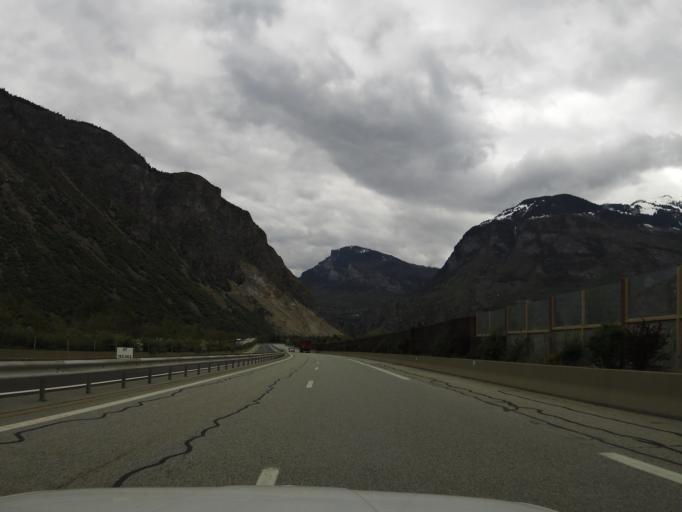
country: FR
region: Rhone-Alpes
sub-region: Departement de la Savoie
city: Saint-Jean-de-Maurienne
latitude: 45.2815
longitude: 6.3571
